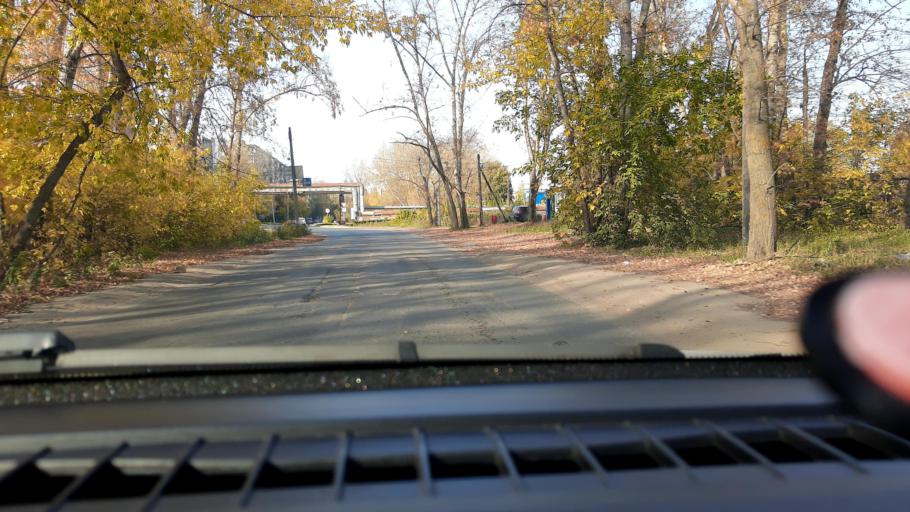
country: RU
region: Nizjnij Novgorod
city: Burevestnik
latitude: 56.2276
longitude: 43.8858
